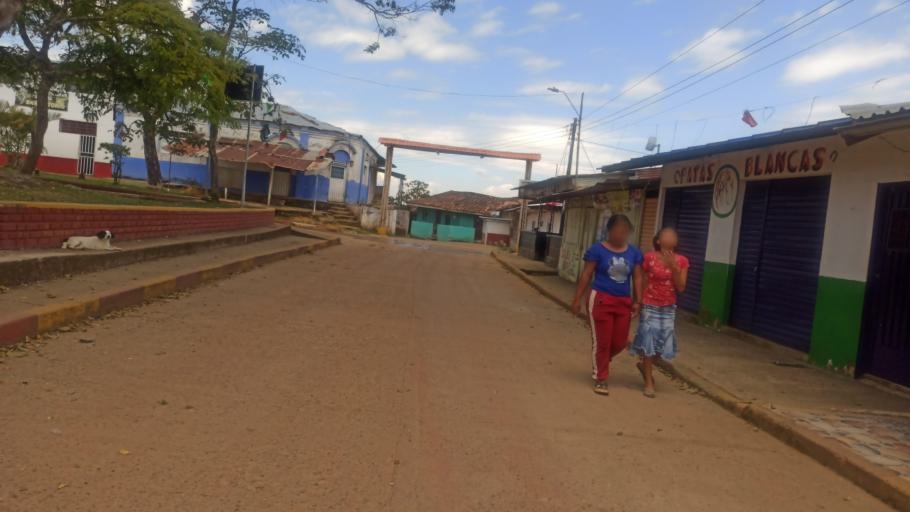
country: CO
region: Valle del Cauca
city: Jamundi
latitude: 3.2095
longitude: -76.6535
